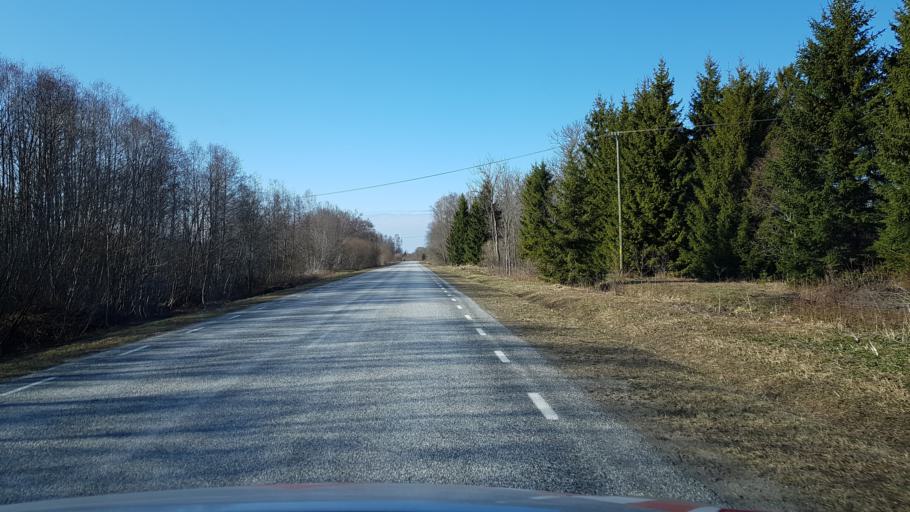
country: EE
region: Laeaene-Virumaa
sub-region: Haljala vald
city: Haljala
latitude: 59.4901
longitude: 26.1463
